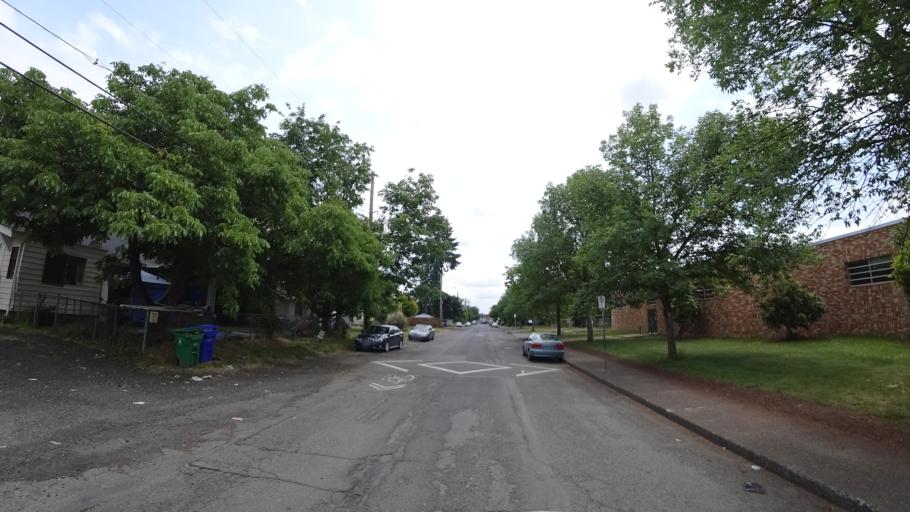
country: US
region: Oregon
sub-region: Multnomah County
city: Lents
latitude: 45.5064
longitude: -122.5743
